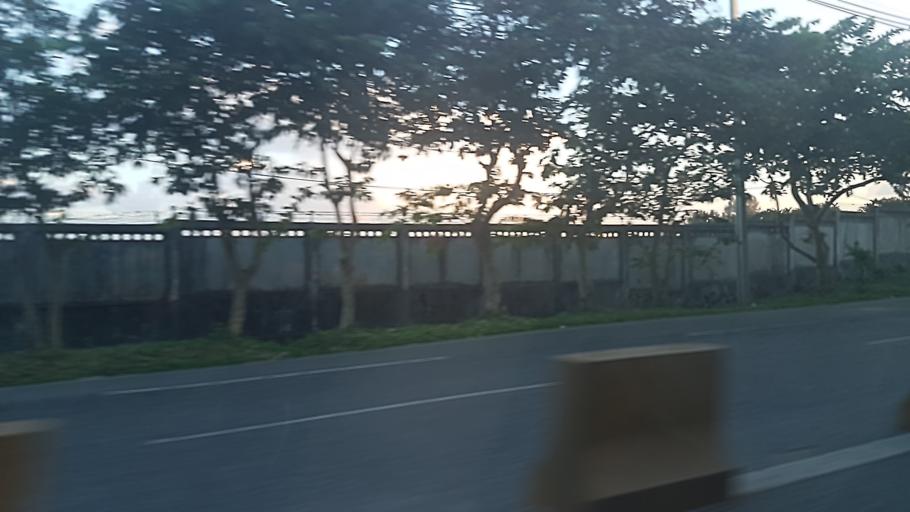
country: MM
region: Yangon
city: Yangon
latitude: 16.9108
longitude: 96.1318
